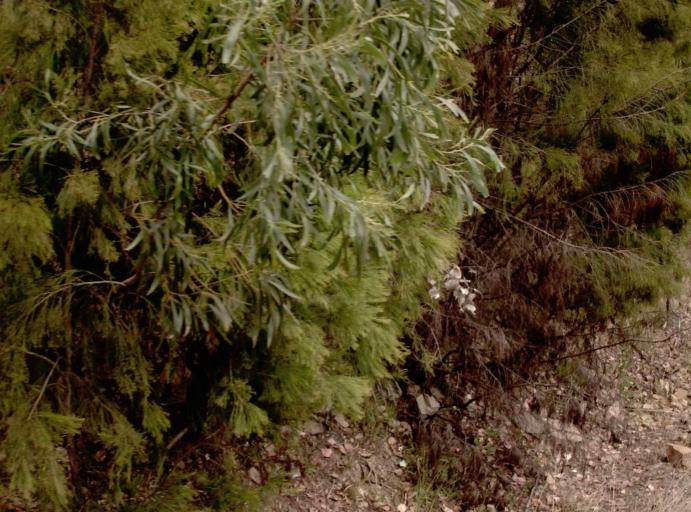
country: AU
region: Victoria
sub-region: Wellington
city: Heyfield
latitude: -37.7829
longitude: 146.6668
